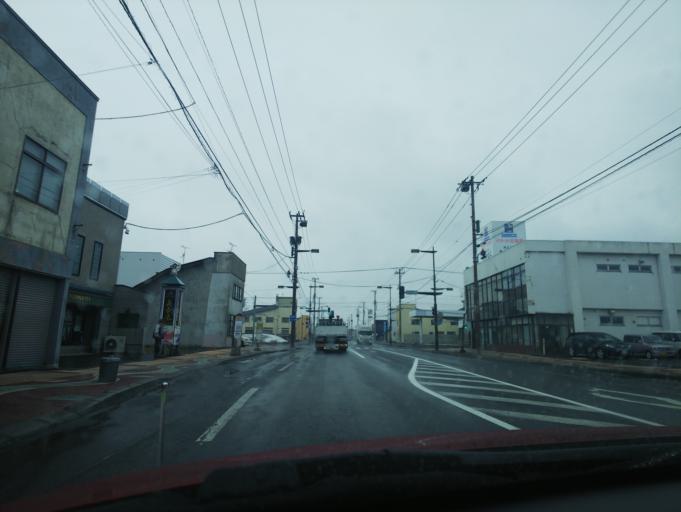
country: JP
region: Hokkaido
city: Nayoro
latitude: 44.1802
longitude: 142.3910
